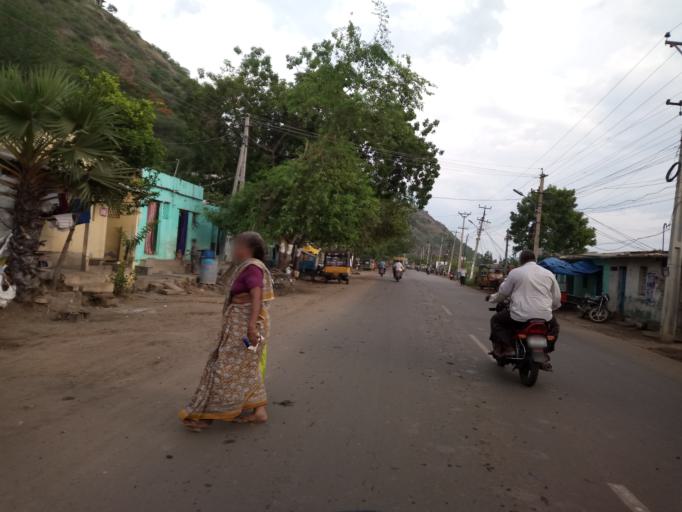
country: IN
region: Andhra Pradesh
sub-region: Guntur
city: Tadepalle
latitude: 16.4974
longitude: 80.6020
